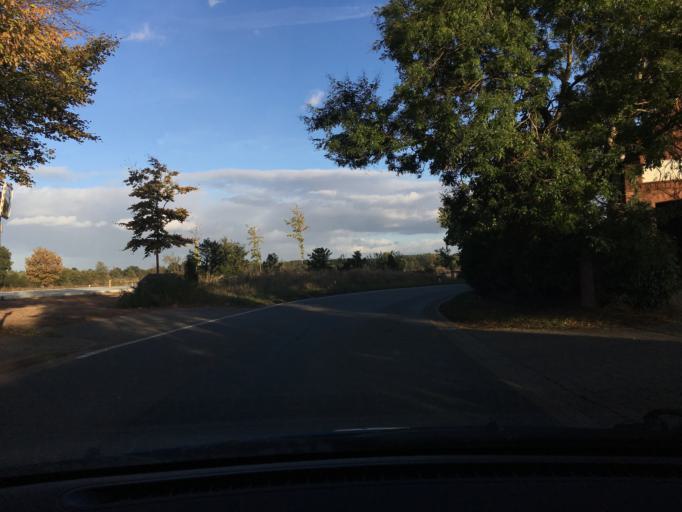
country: DE
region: Lower Saxony
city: Hittbergen
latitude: 53.3439
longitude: 10.5977
